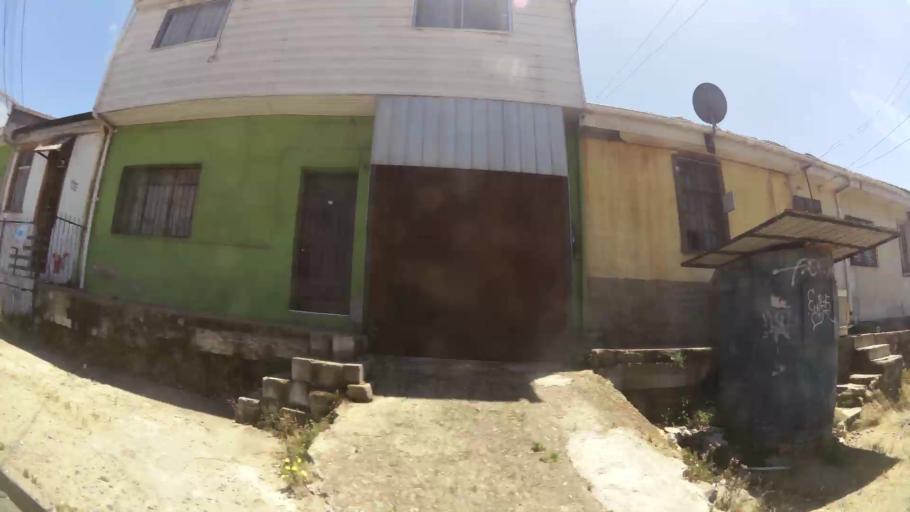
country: CL
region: Valparaiso
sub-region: Provincia de Valparaiso
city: Valparaiso
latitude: -33.0406
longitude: -71.6363
